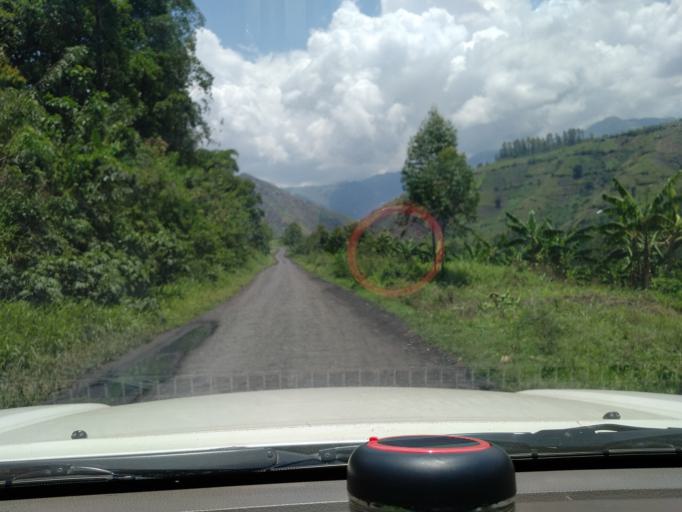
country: CD
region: Nord Kivu
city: Sake
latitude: -1.7389
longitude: 29.0025
